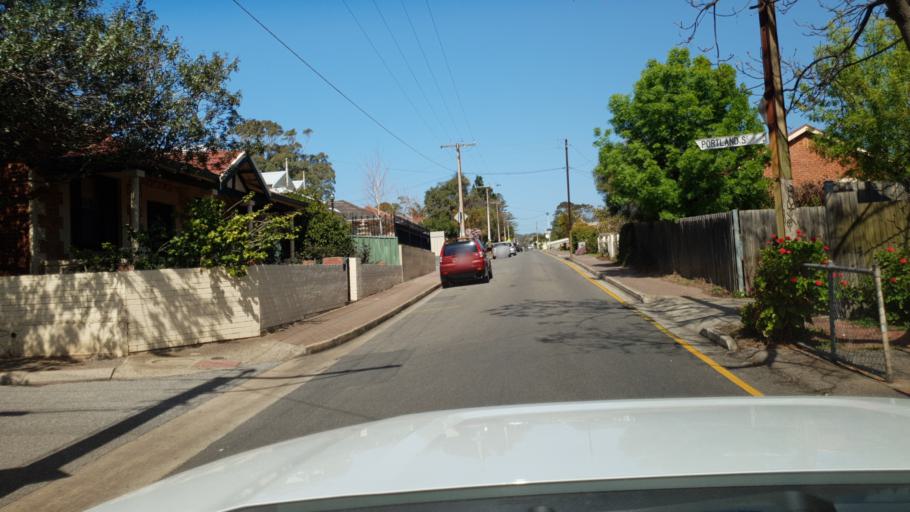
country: AU
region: South Australia
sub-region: Adelaide Hills
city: Seacliff
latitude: -35.0287
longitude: 138.5220
